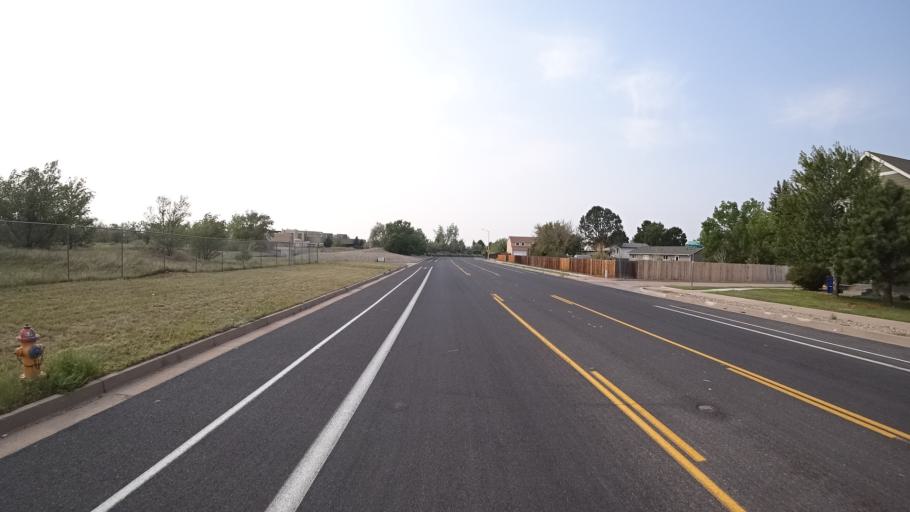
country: US
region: Colorado
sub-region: El Paso County
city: Cimarron Hills
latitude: 38.8110
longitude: -104.7336
